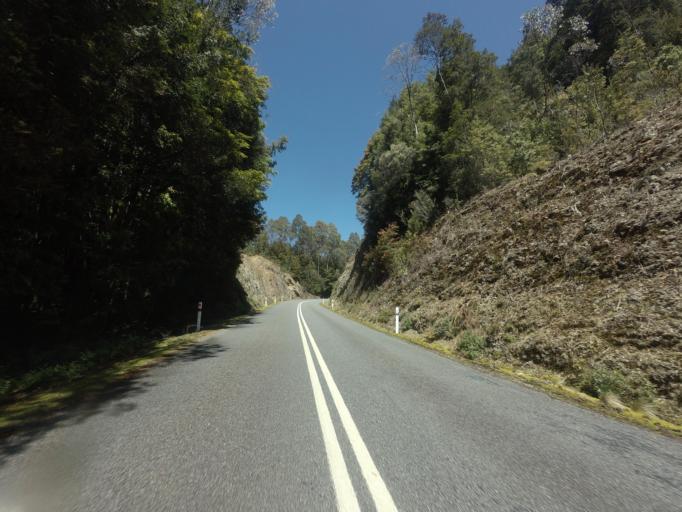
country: AU
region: Tasmania
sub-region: Huon Valley
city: Geeveston
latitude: -42.8156
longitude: 146.3677
